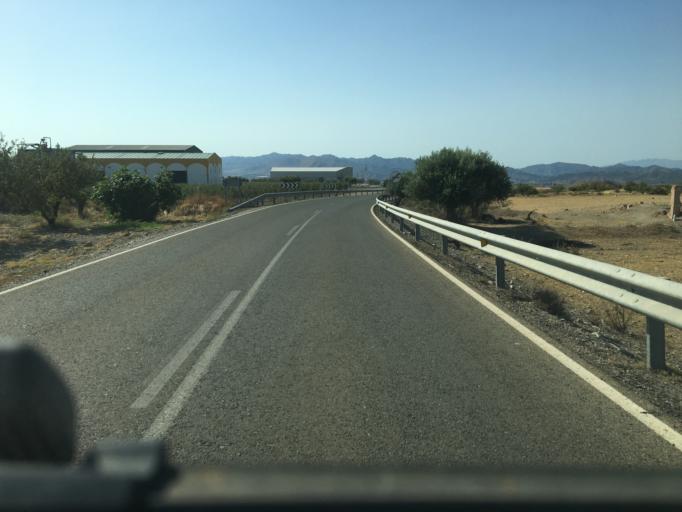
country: ES
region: Andalusia
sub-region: Provincia de Almeria
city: Huercal-Overa
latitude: 37.4416
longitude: -1.9785
